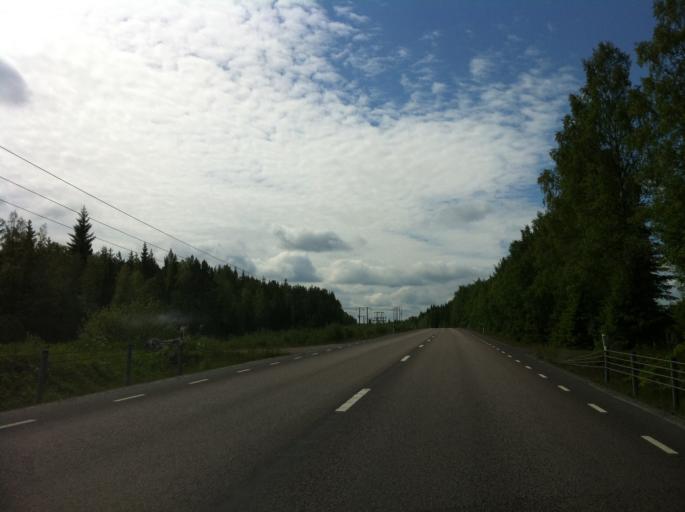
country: SE
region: Vaermland
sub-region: Karlstads Kommun
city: Edsvalla
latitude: 59.4206
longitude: 13.1899
